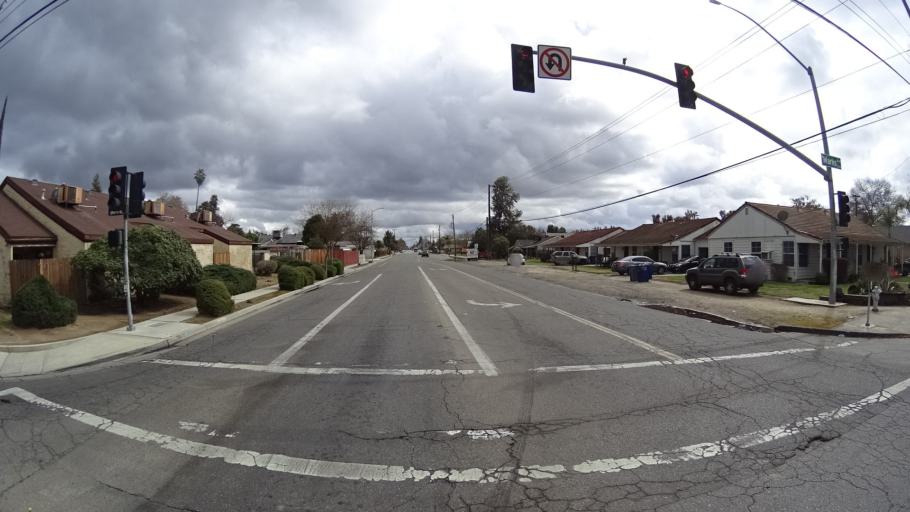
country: US
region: California
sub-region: Fresno County
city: West Park
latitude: 36.7864
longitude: -119.8444
